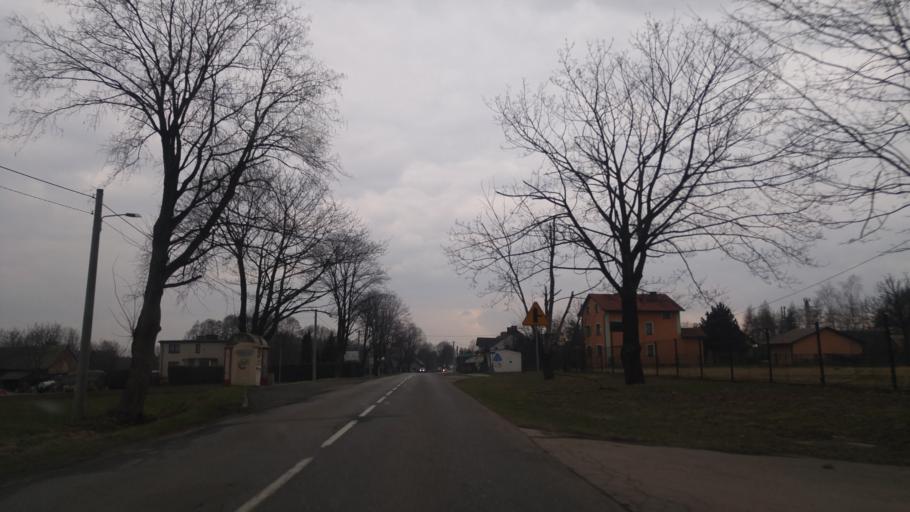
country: PL
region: Silesian Voivodeship
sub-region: Powiat cieszynski
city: Zablocie
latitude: 49.9322
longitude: 18.8009
